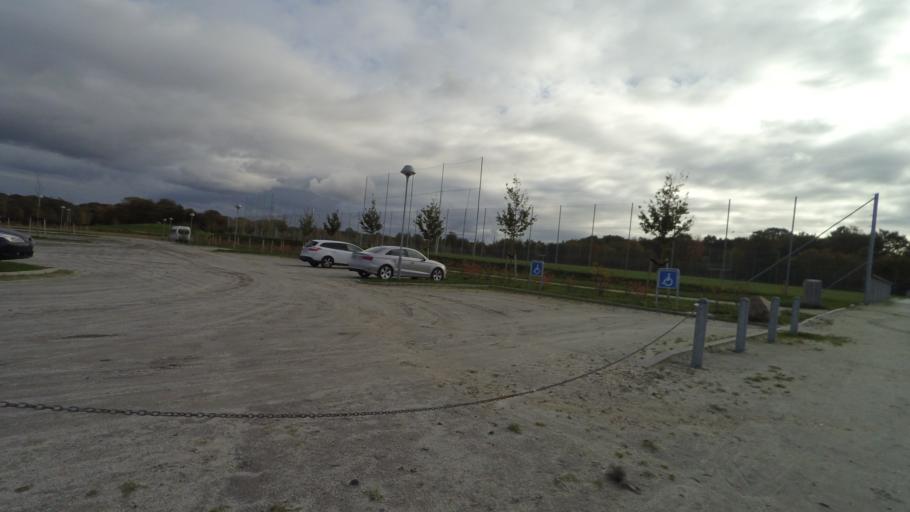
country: DK
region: Central Jutland
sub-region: Arhus Kommune
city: Stavtrup
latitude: 56.1196
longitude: 10.1275
